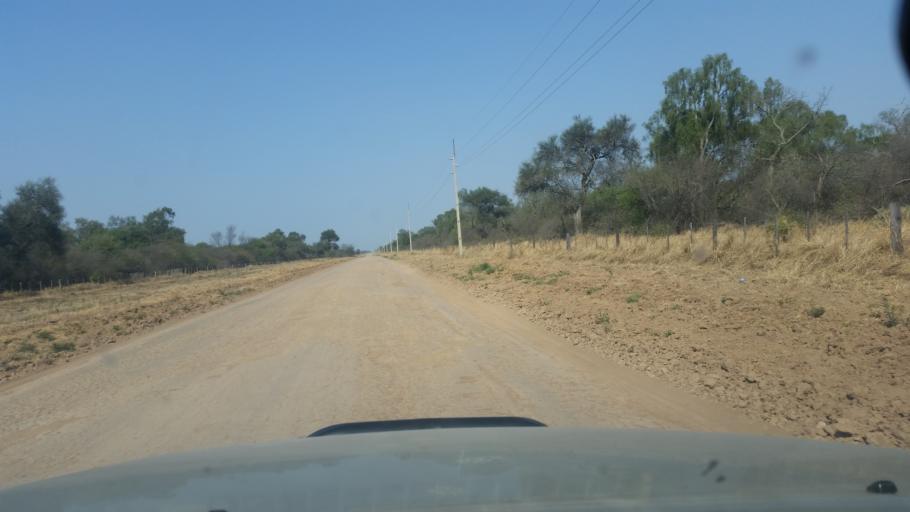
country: PY
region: Boqueron
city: Filadelfia
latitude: -22.0744
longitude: -60.7182
